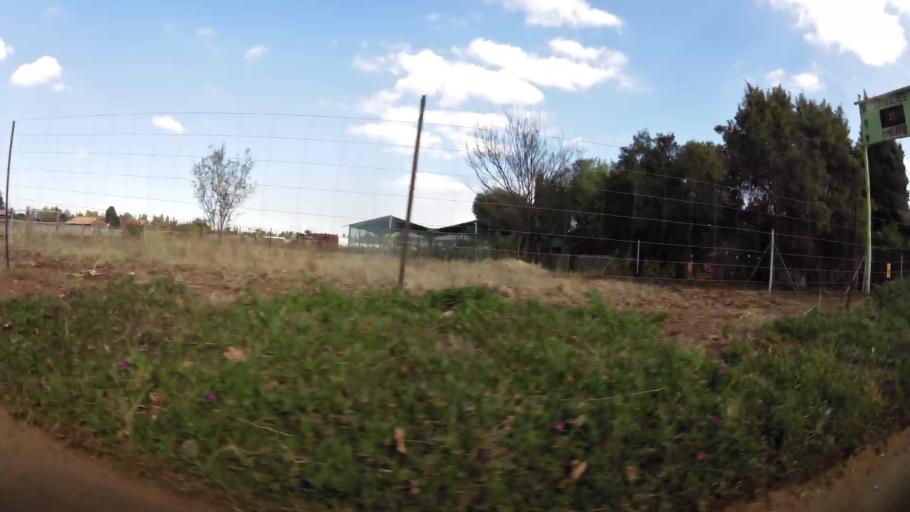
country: ZA
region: Gauteng
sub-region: Ekurhuleni Metropolitan Municipality
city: Benoni
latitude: -26.1100
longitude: 28.3585
